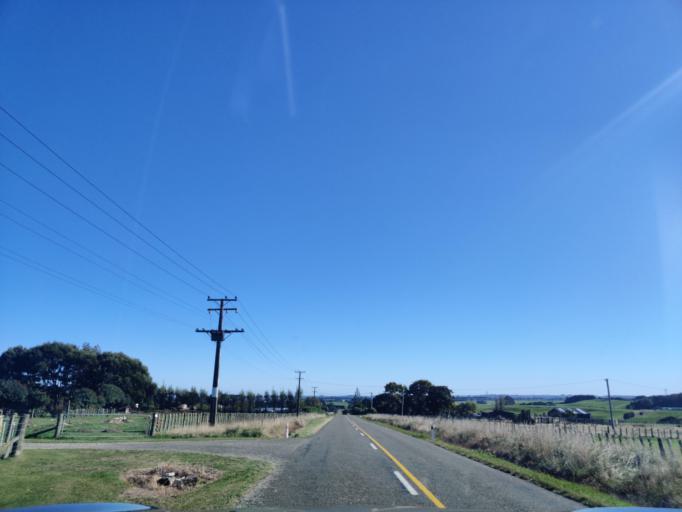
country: NZ
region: Manawatu-Wanganui
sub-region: Palmerston North City
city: Palmerston North
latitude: -40.2445
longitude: 175.6750
